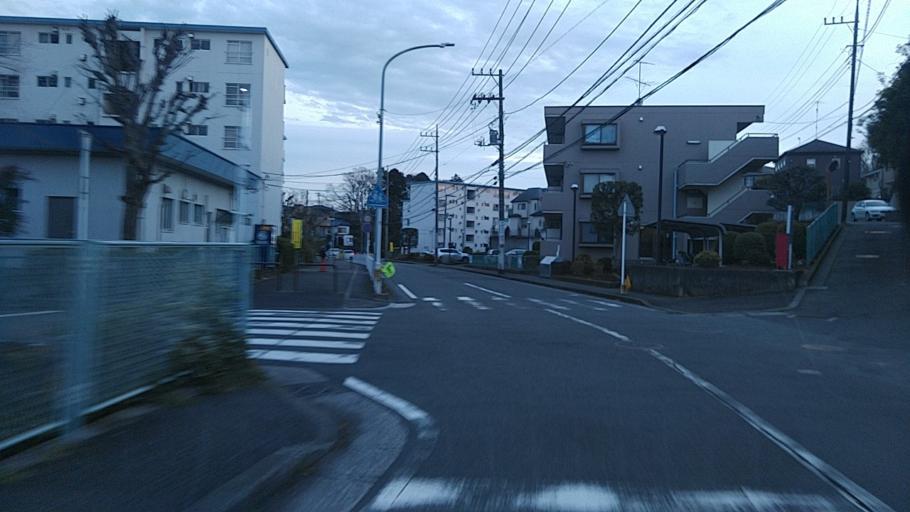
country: JP
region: Kanagawa
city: Fujisawa
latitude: 35.4138
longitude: 139.4920
